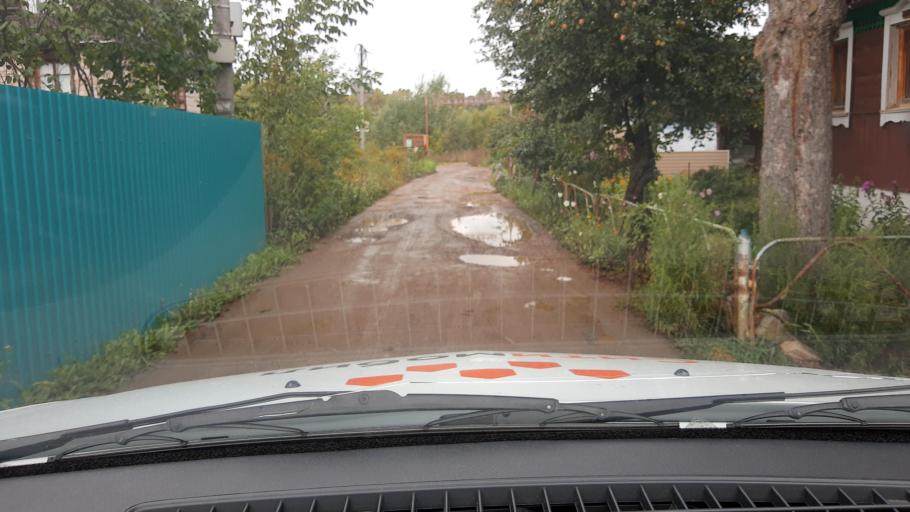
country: RU
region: Bashkortostan
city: Iglino
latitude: 54.7776
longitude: 56.2013
